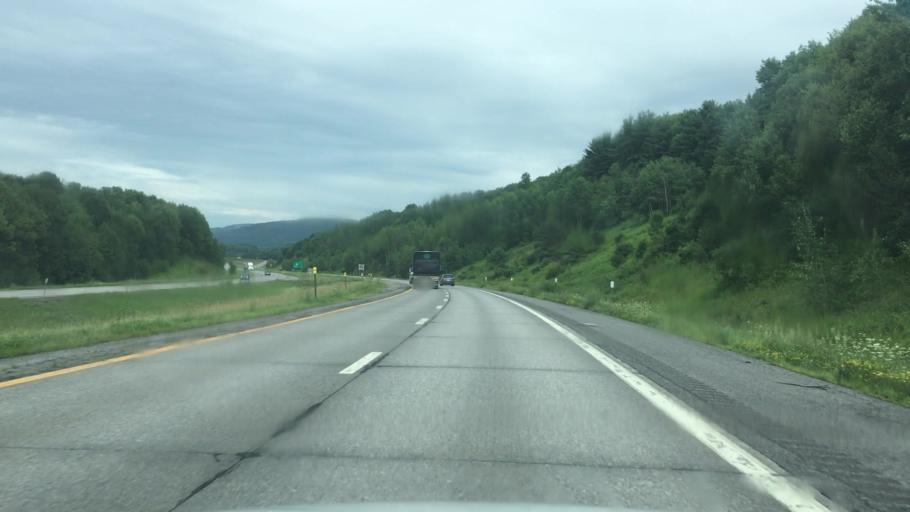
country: US
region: New York
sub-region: Otsego County
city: Worcester
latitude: 42.5870
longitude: -74.7420
